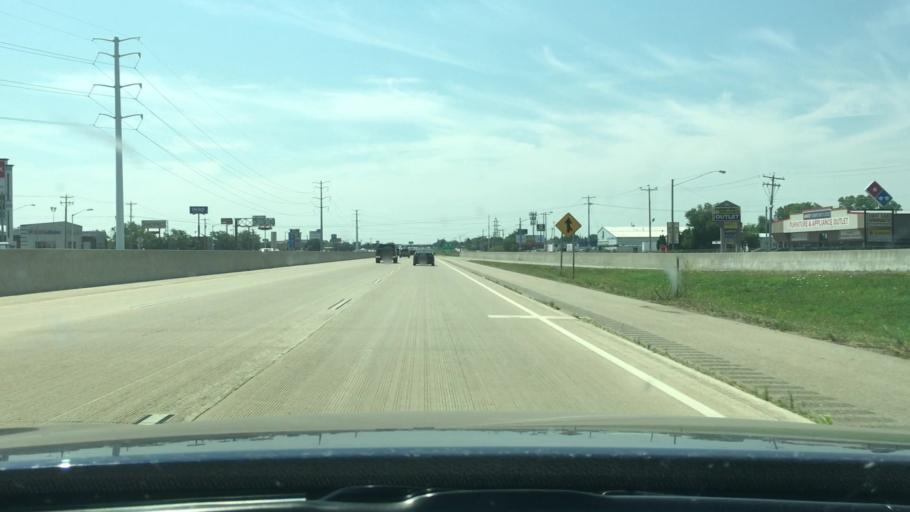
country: US
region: Wisconsin
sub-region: Winnebago County
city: Oshkosh
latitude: 44.0090
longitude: -88.5825
